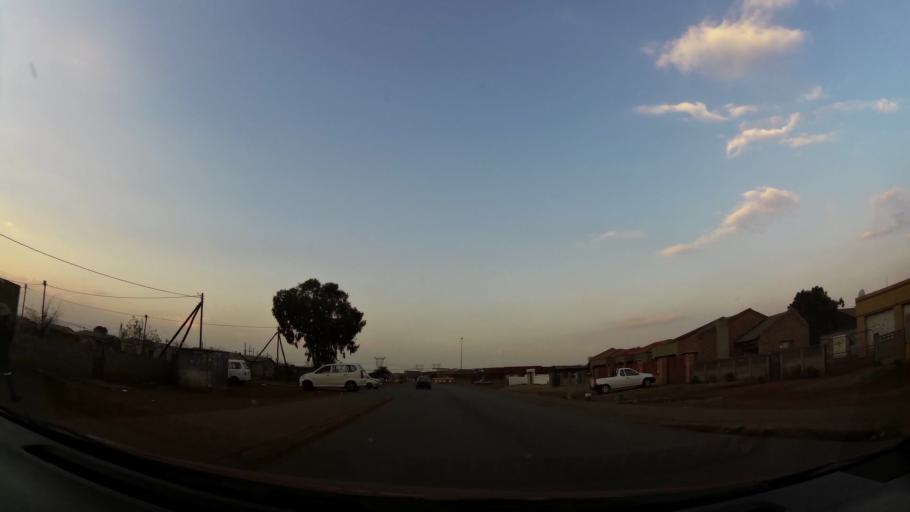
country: ZA
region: Gauteng
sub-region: City of Johannesburg Metropolitan Municipality
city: Orange Farm
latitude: -26.5615
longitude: 27.8538
